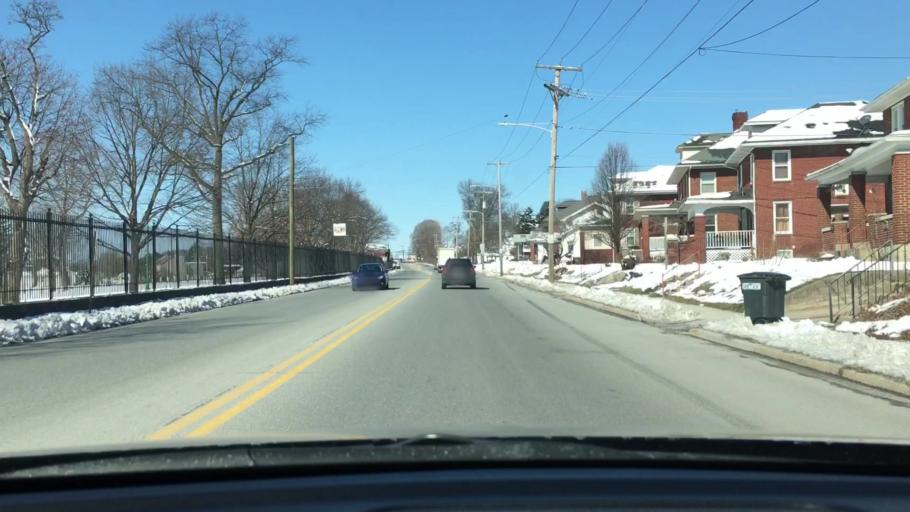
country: US
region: Pennsylvania
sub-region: York County
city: West York
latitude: 39.9600
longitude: -76.7553
